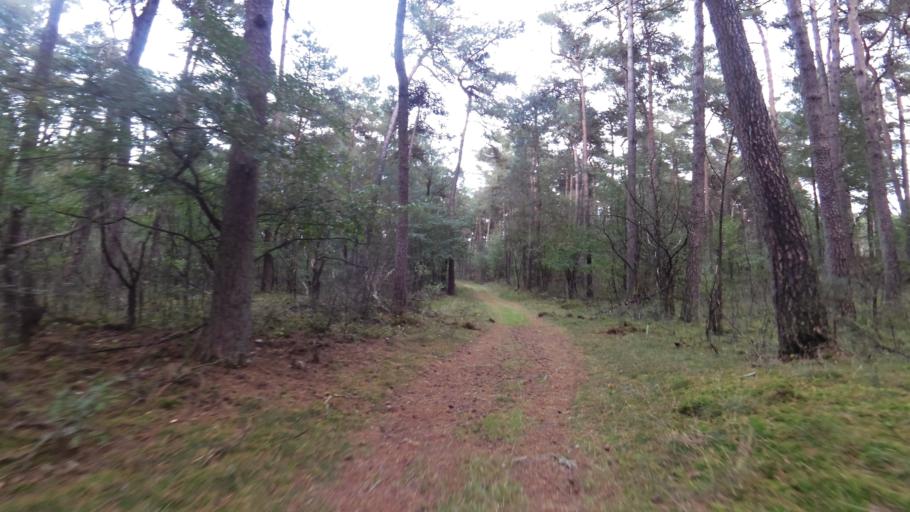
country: NL
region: Gelderland
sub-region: Gemeente Ede
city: Harskamp
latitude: 52.1564
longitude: 5.7497
